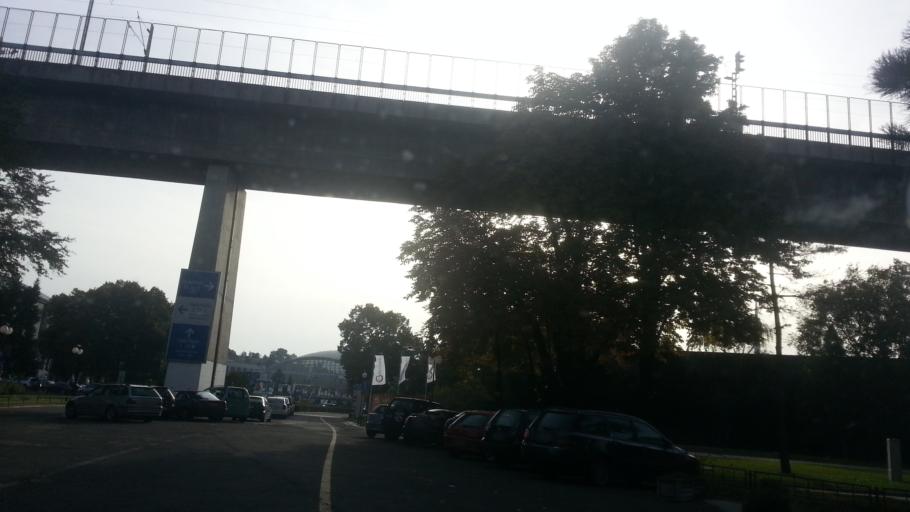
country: RS
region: Central Serbia
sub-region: Belgrade
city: Novi Beograd
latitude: 44.7983
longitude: 20.4395
